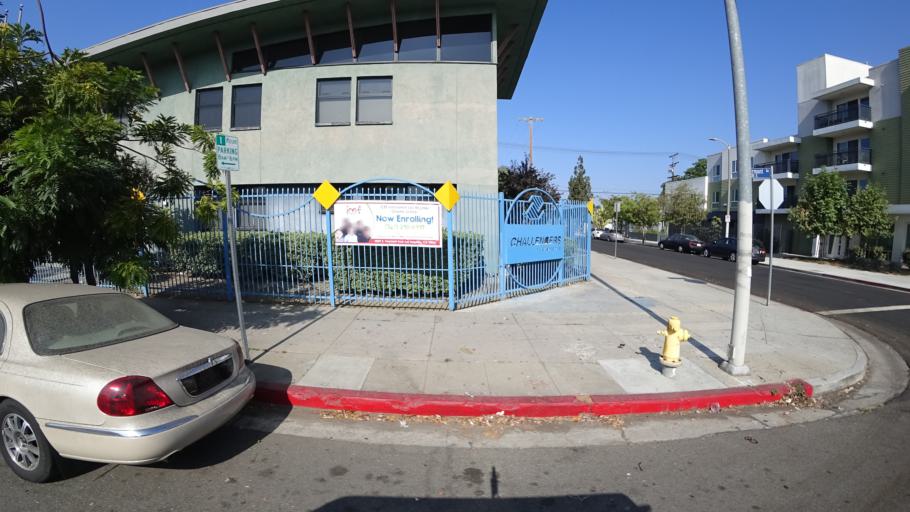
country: US
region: California
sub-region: Los Angeles County
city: Florence-Graham
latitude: 33.9978
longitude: -118.2916
